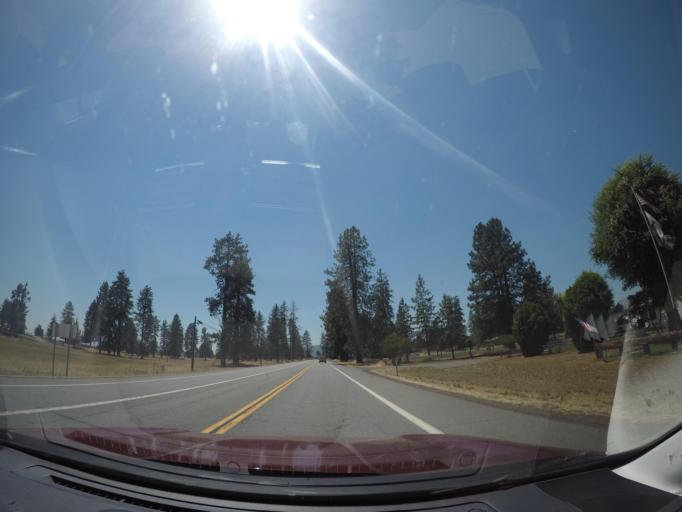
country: US
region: California
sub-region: Shasta County
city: Burney
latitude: 41.0580
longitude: -121.3789
